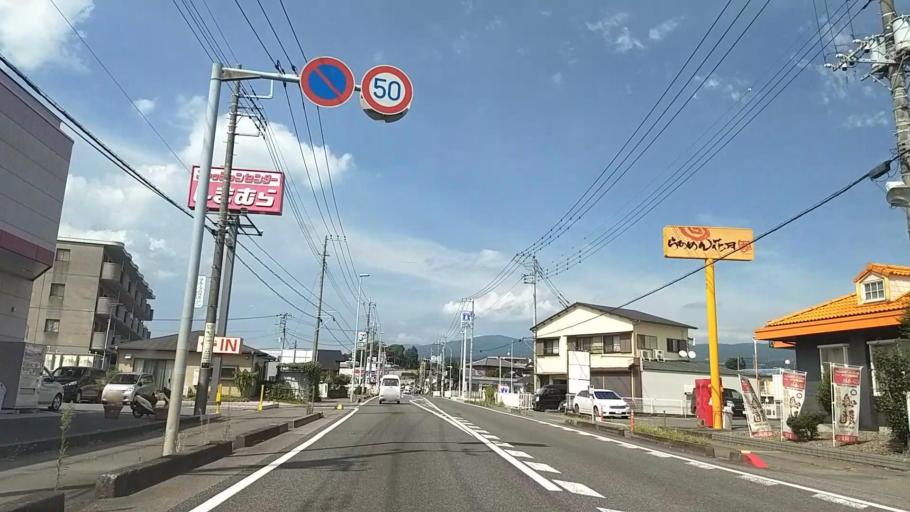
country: JP
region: Shizuoka
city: Mishima
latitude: 35.1158
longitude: 138.9283
